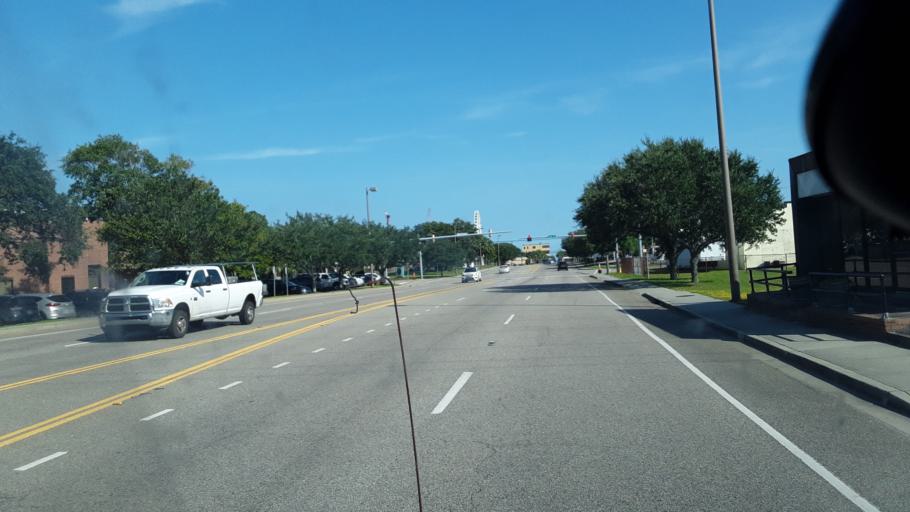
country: US
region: South Carolina
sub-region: Horry County
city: Myrtle Beach
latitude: 33.6976
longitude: -78.8830
